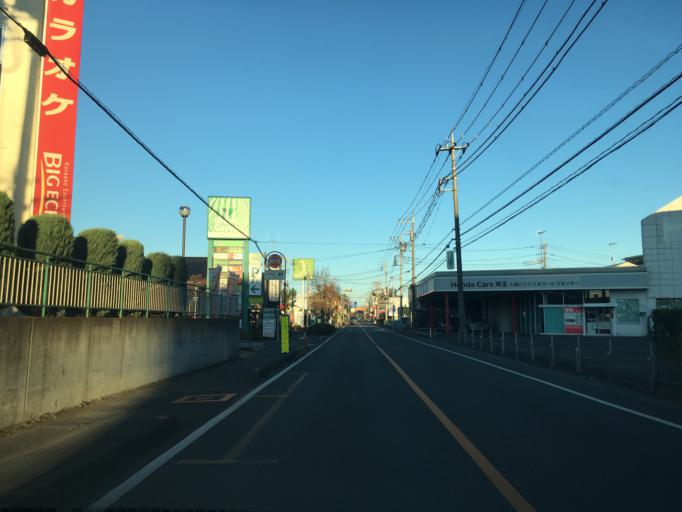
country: JP
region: Saitama
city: Sayama
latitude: 35.8206
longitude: 139.4156
